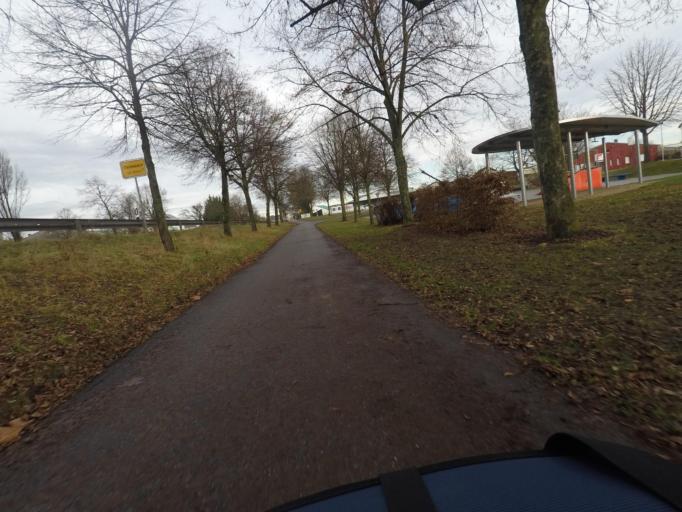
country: DE
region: Baden-Wuerttemberg
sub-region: Karlsruhe Region
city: Steinmauern
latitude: 48.8927
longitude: 8.1945
